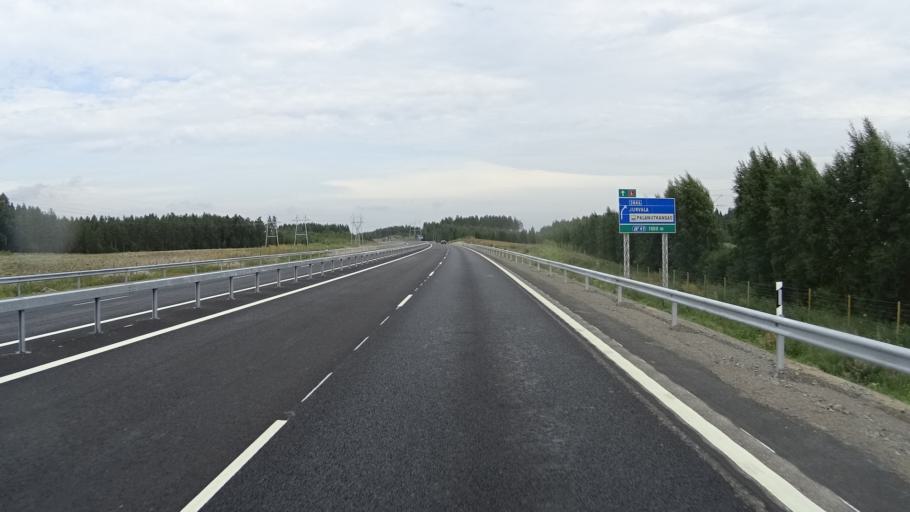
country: FI
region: South Karelia
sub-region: Lappeenranta
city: Lemi
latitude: 60.9646
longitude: 27.8527
